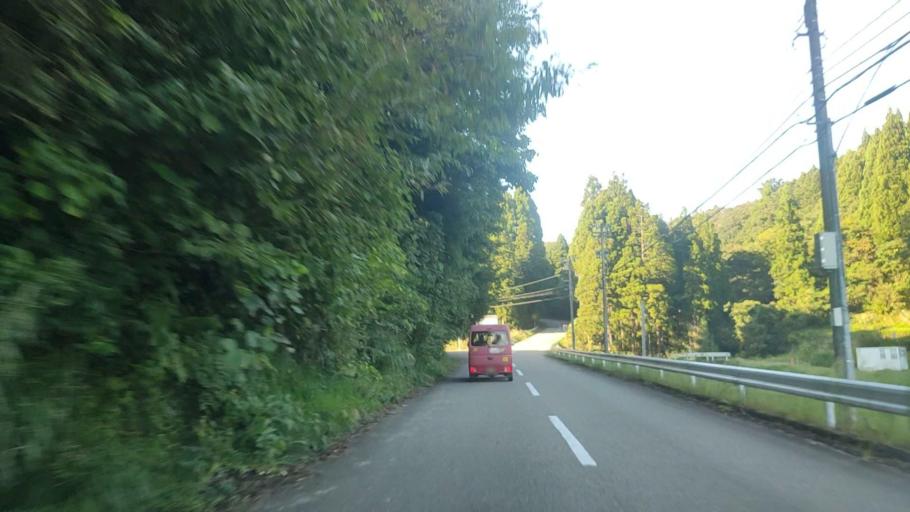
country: JP
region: Ishikawa
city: Nanao
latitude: 37.1086
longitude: 136.9618
